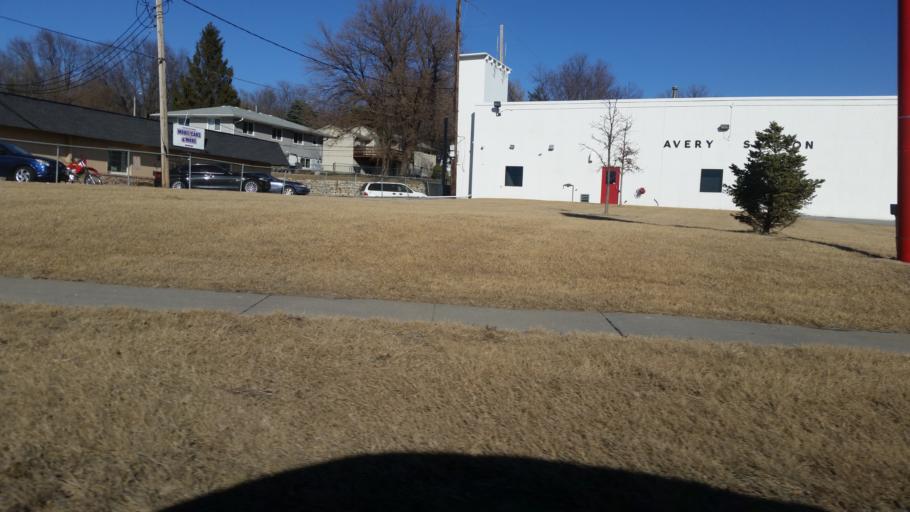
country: US
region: Nebraska
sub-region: Sarpy County
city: Bellevue
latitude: 41.1662
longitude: -95.9241
